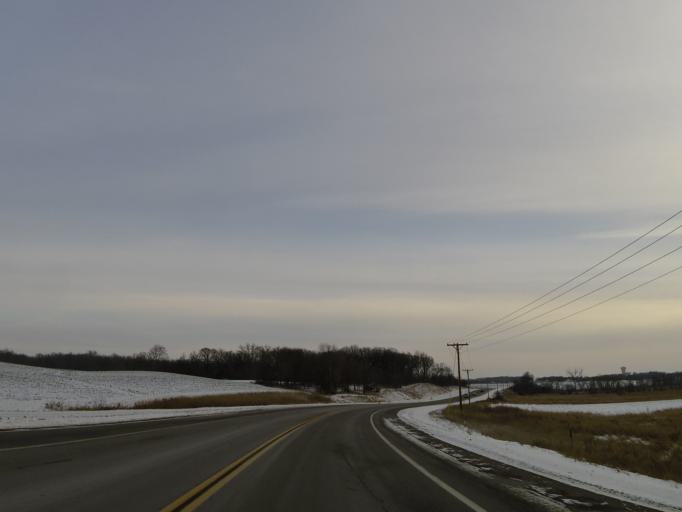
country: US
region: Minnesota
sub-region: Carver County
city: Carver
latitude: 44.8015
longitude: -93.6475
